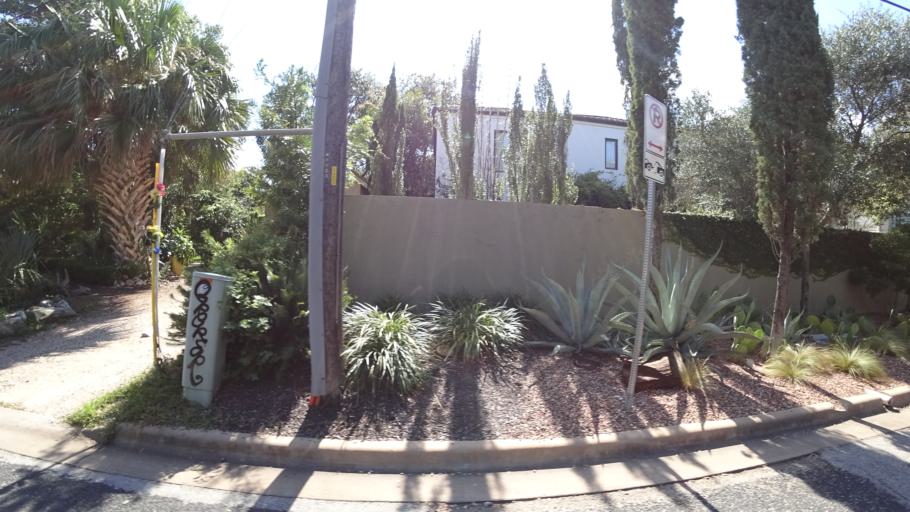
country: US
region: Texas
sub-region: Travis County
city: Austin
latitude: 30.3013
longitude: -97.7478
